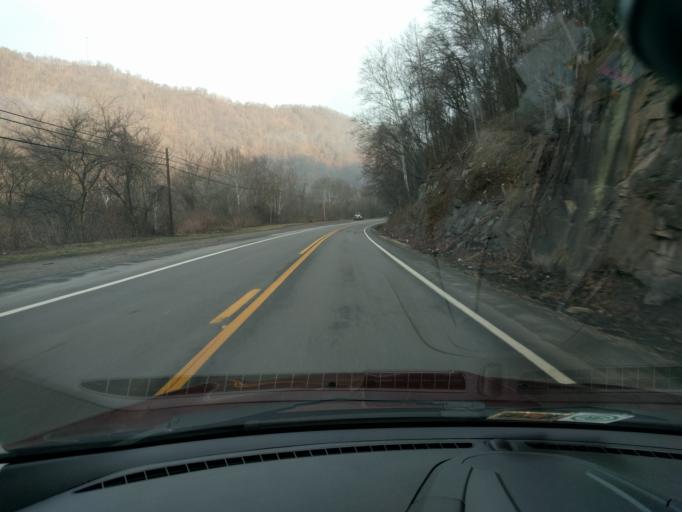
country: US
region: West Virginia
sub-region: Kanawha County
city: Montgomery
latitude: 38.1614
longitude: -81.2998
